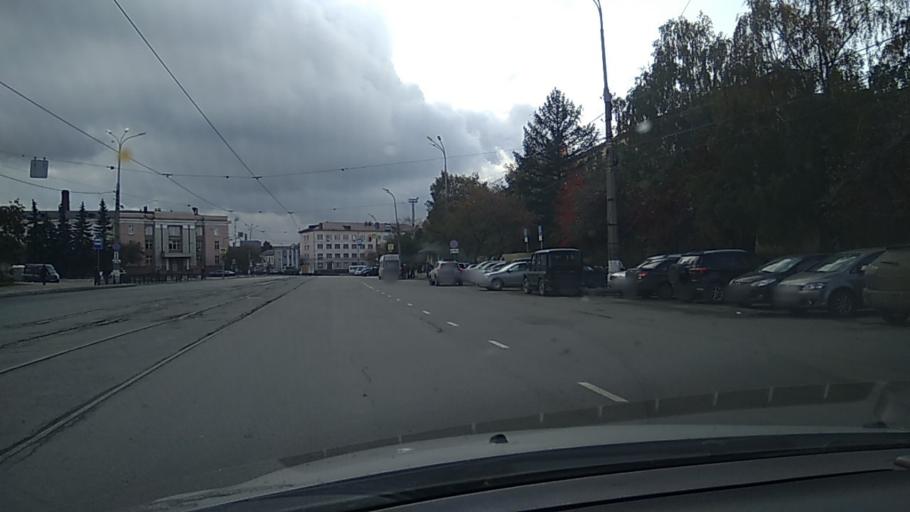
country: RU
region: Sverdlovsk
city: Nizhniy Tagil
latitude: 57.9296
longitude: 60.0126
